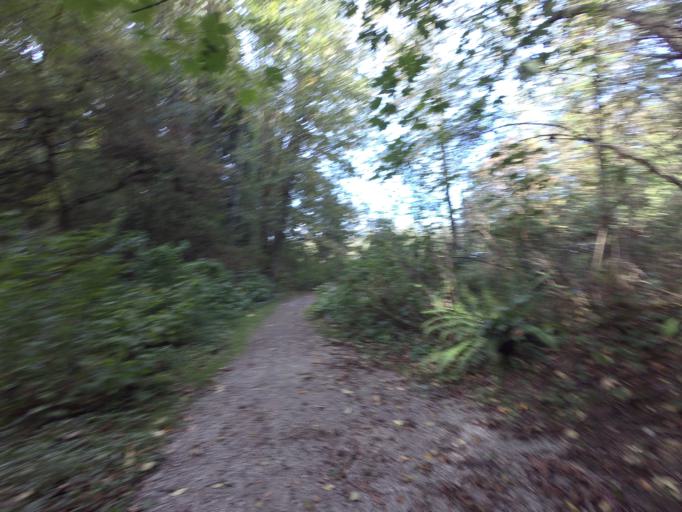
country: CA
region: British Columbia
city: New Westminster
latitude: 49.2346
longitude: -122.8916
